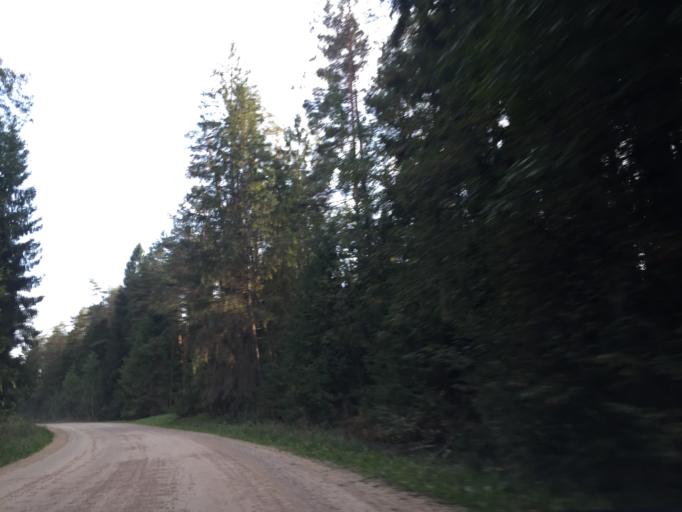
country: LV
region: Baldone
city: Baldone
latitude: 56.7959
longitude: 24.4375
